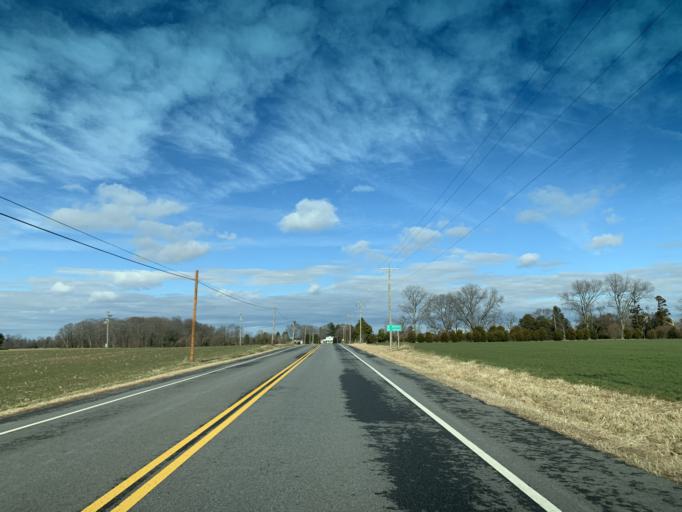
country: US
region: Maryland
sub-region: Kent County
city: Chestertown
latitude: 39.3422
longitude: -76.0622
